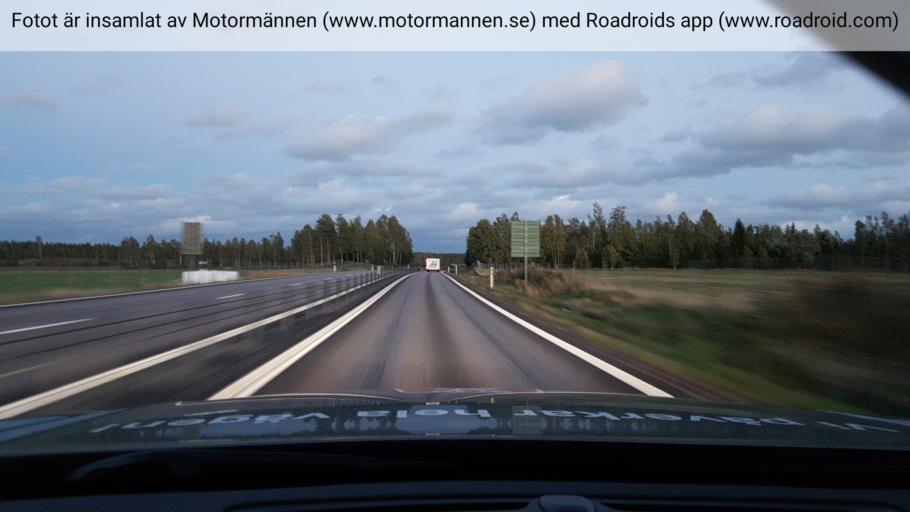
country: SE
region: Vaermland
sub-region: Karlstads Kommun
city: Skattkarr
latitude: 59.4144
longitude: 13.7468
